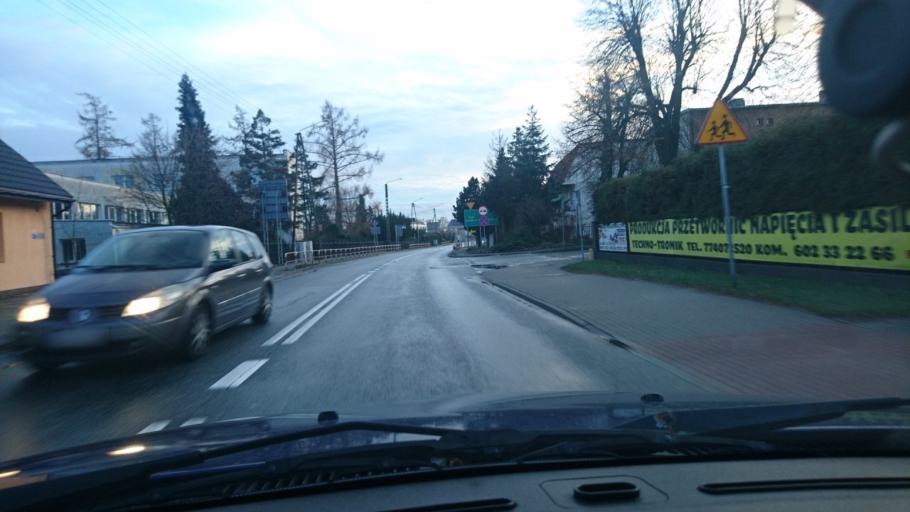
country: PL
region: Opole Voivodeship
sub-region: Powiat kluczborski
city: Byczyna
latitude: 51.1156
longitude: 18.2094
